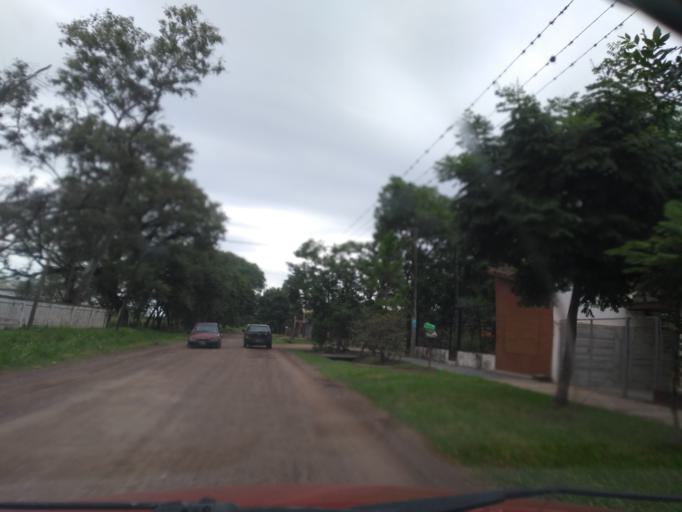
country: AR
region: Chaco
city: Barranqueras
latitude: -27.4779
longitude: -58.9593
